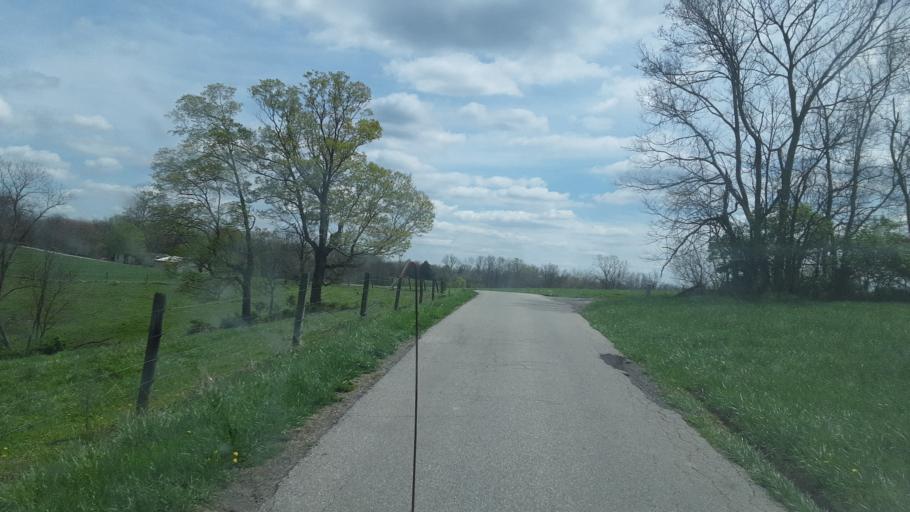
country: US
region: Kentucky
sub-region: Owen County
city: Owenton
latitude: 38.6649
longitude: -84.7779
